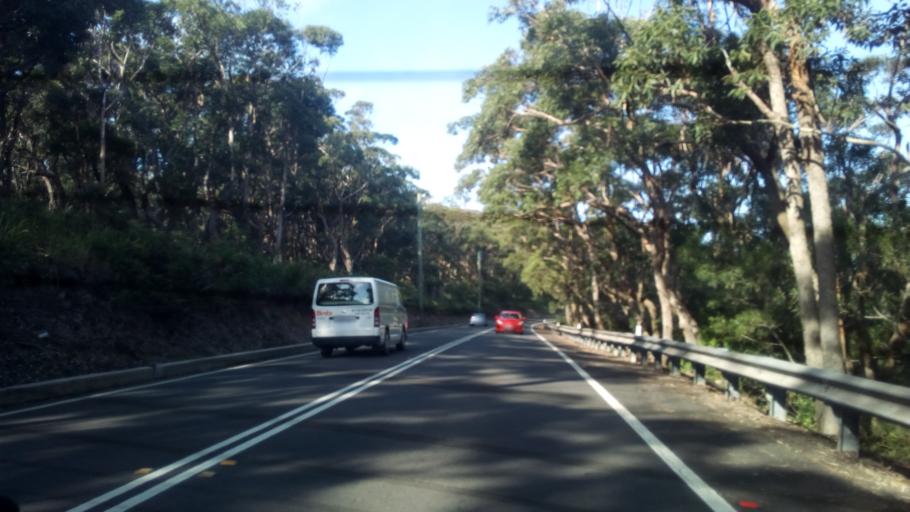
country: AU
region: New South Wales
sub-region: Wollongong
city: Helensburgh
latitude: -34.2213
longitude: 150.9916
